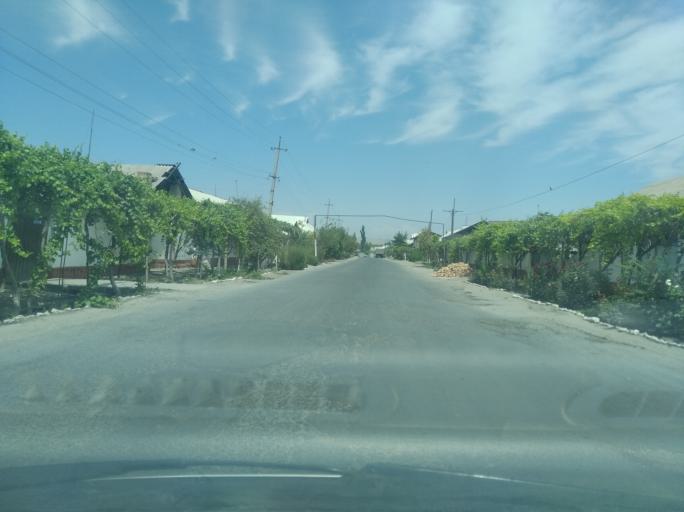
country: KG
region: Osh
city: Aravan
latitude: 40.6146
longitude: 72.4553
